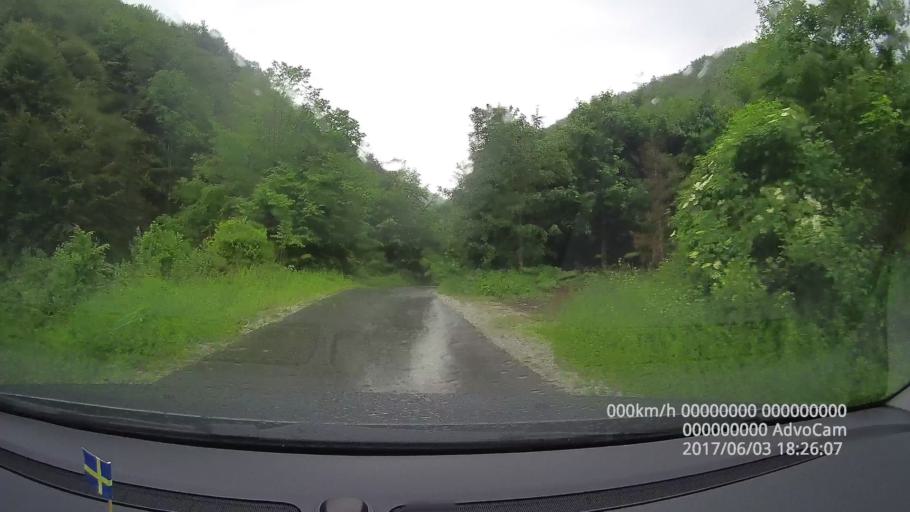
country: RO
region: Gorj
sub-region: Comuna Runcu
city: Dobrita
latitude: 45.1711
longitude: 23.1913
